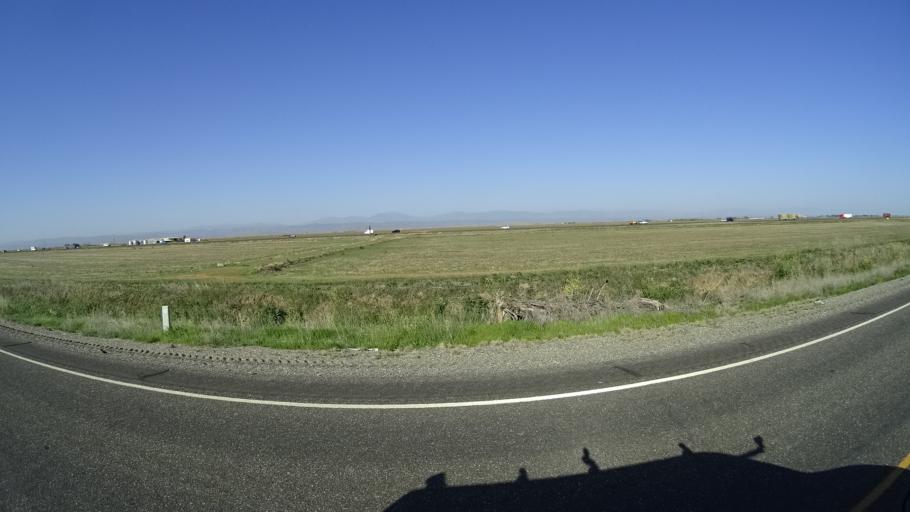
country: US
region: California
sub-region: Glenn County
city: Willows
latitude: 39.4753
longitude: -122.1930
